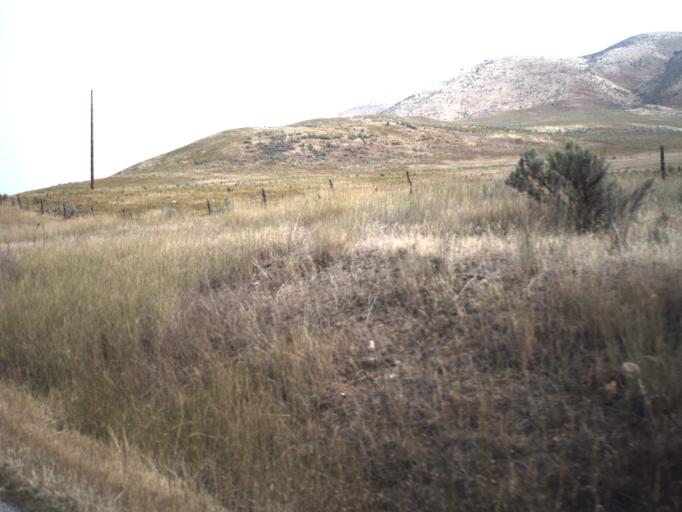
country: US
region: Utah
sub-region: Summit County
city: Coalville
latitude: 40.9931
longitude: -111.5251
